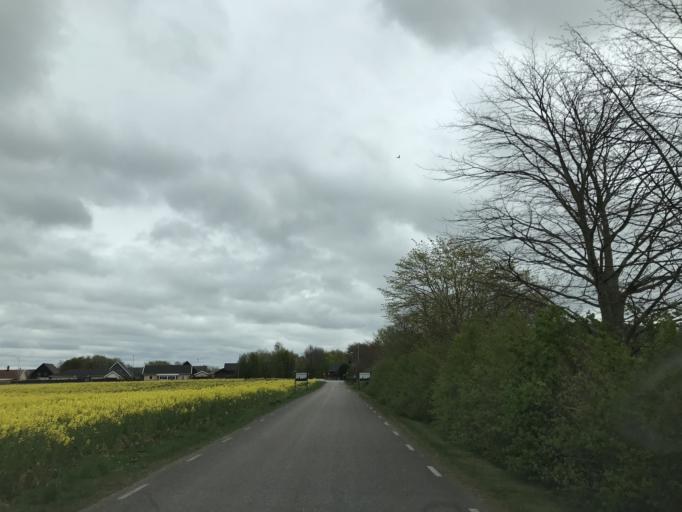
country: SE
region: Skane
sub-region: Svalovs Kommun
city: Teckomatorp
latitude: 55.8645
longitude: 13.0796
